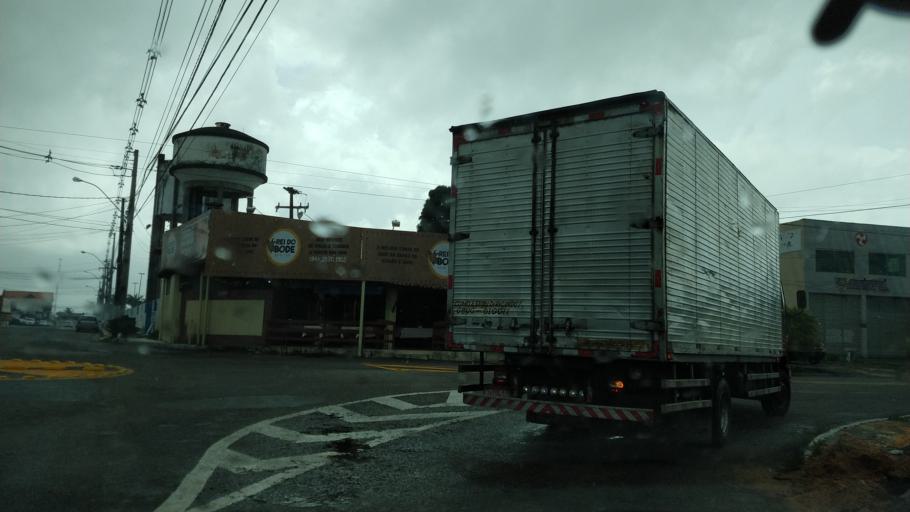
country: BR
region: Rio Grande do Norte
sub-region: Parnamirim
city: Parnamirim
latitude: -5.9213
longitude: -35.2695
